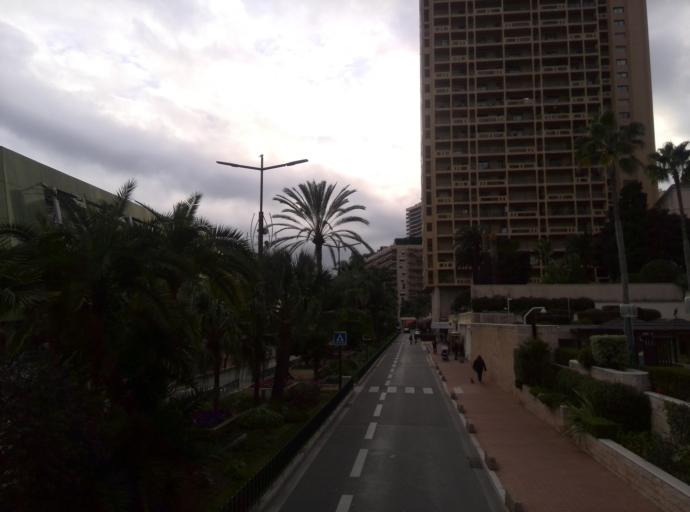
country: MC
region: Commune de Monaco
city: Saint-Roman
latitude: 43.7448
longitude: 7.4314
